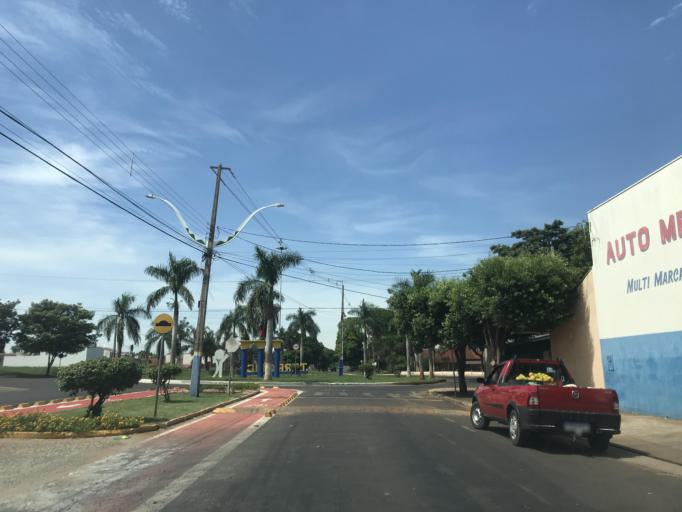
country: BR
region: Parana
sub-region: Terra Rica
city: Terra Rica
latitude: -22.7339
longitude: -52.6246
